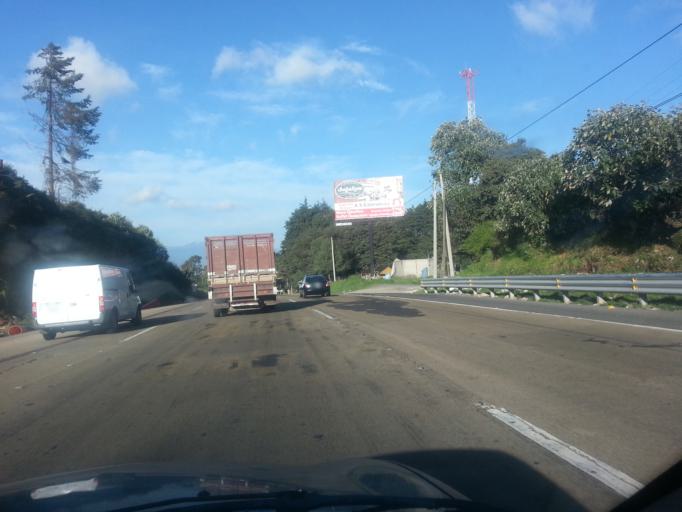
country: MX
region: Mexico
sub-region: Lerma
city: San Miguel Ameyalco
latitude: 19.2920
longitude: -99.4320
